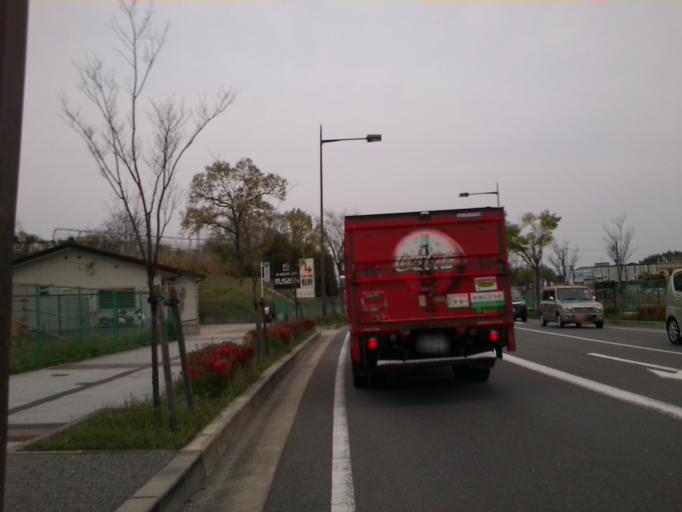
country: JP
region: Kyoto
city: Yawata
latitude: 34.8427
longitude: 135.7135
